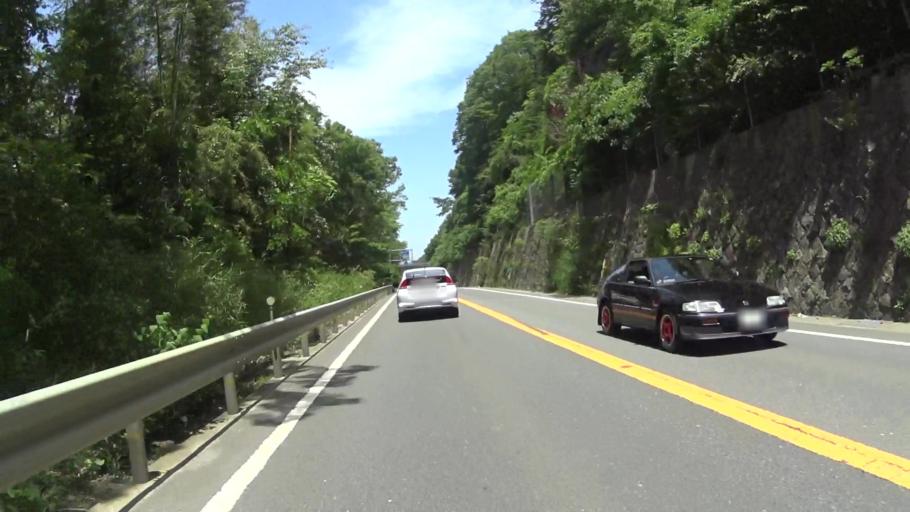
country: JP
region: Kyoto
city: Kameoka
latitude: 35.1449
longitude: 135.4272
